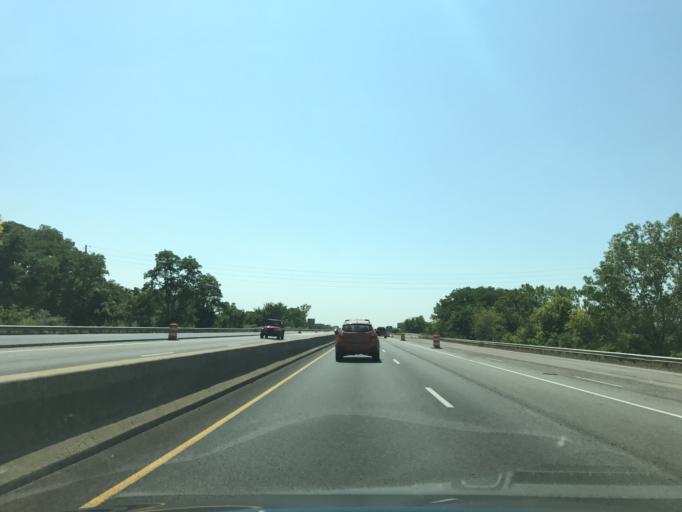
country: US
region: Indiana
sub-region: Porter County
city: Porter
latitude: 41.6180
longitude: -87.0807
